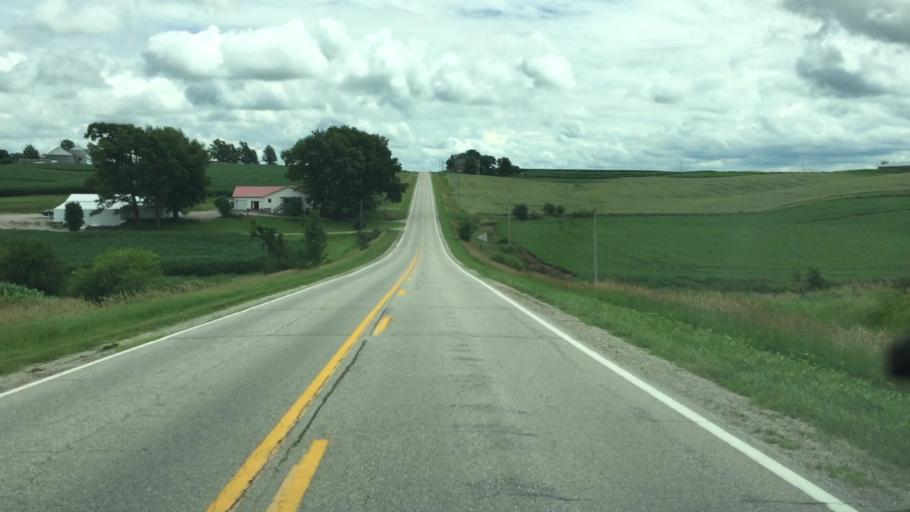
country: US
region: Iowa
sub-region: Jasper County
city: Monroe
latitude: 41.5736
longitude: -93.0810
